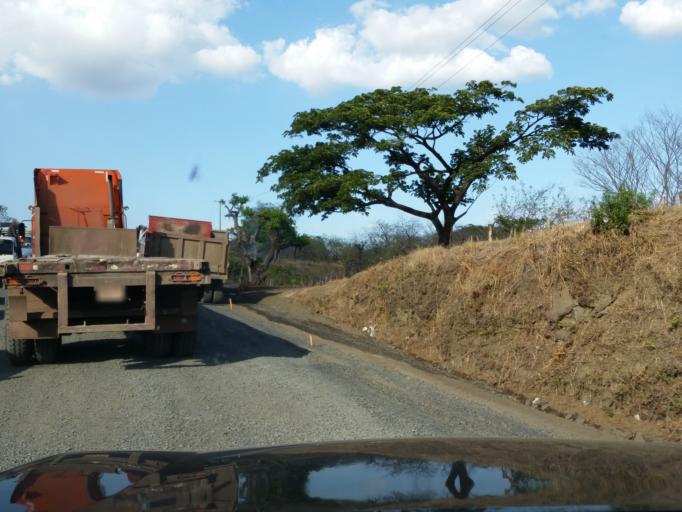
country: NI
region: Managua
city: Carlos Fonseca Amador
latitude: 12.0663
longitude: -86.4466
